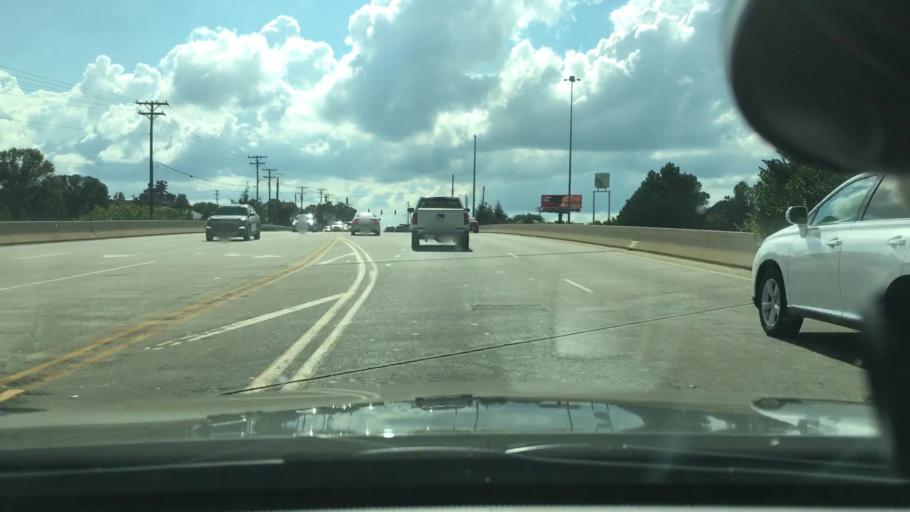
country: US
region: North Carolina
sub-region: Alamance County
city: Elon
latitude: 36.0678
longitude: -79.4979
